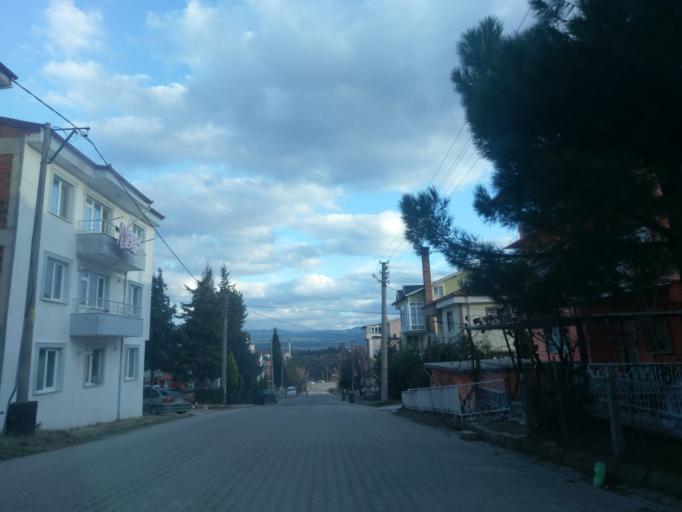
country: TR
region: Kuetahya
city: Gediz
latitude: 38.9892
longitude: 29.3847
